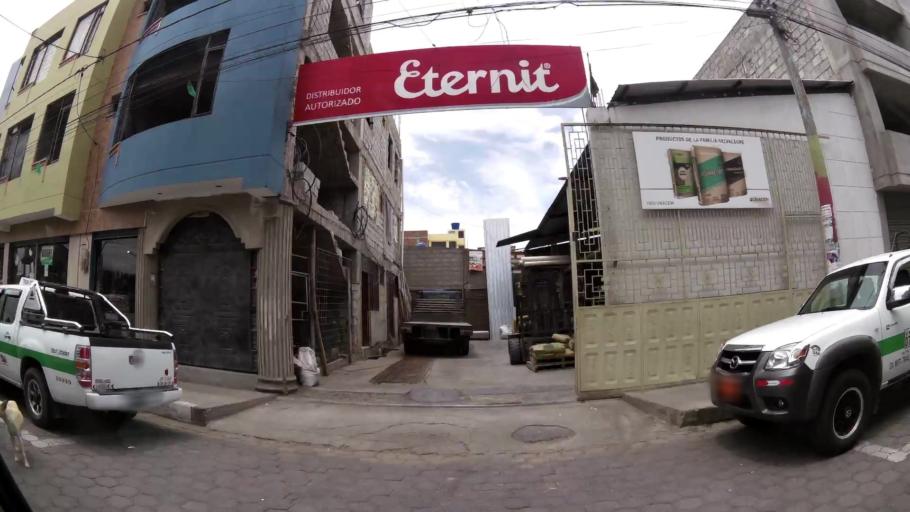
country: EC
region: Cotopaxi
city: San Miguel de Salcedo
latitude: -1.0425
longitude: -78.5857
